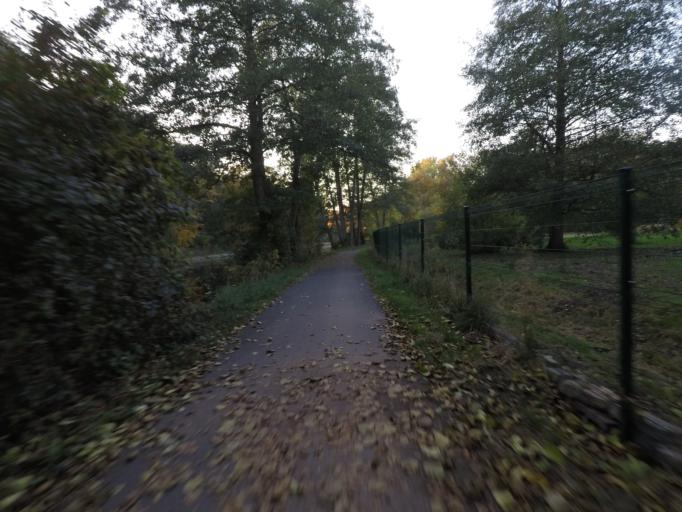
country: DE
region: Brandenburg
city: Melchow
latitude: 52.8453
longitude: 13.7074
